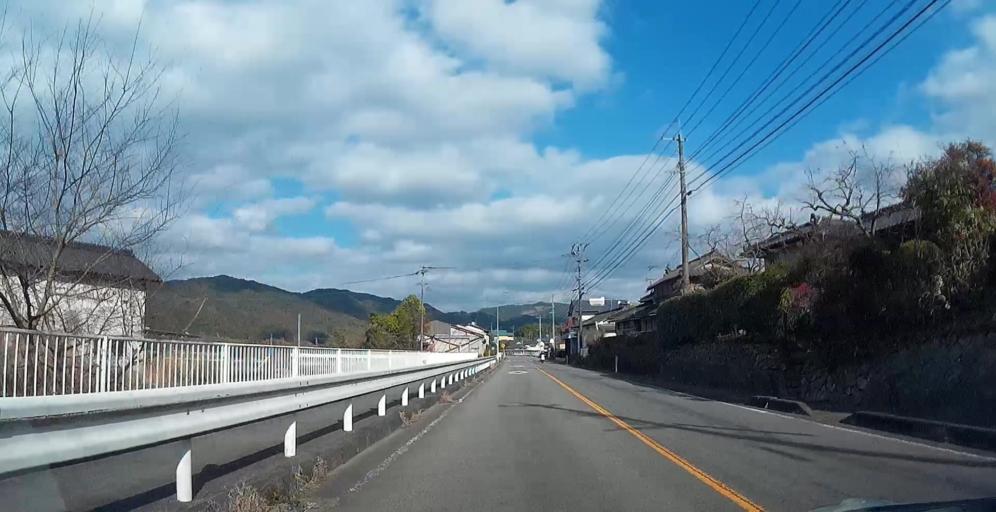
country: JP
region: Kumamoto
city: Yatsushiro
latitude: 32.3988
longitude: 130.5521
